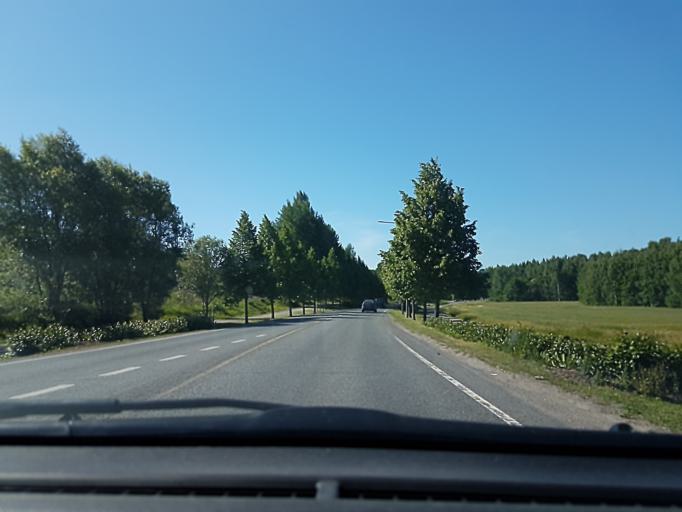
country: FI
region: Uusimaa
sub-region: Helsinki
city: Vantaa
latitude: 60.3447
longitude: 25.0741
